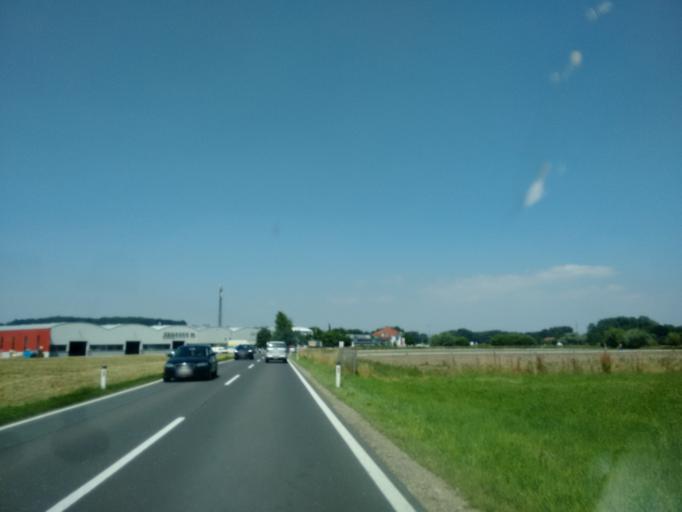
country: AT
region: Upper Austria
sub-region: Wels-Land
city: Buchkirchen
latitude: 48.2689
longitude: 13.9874
